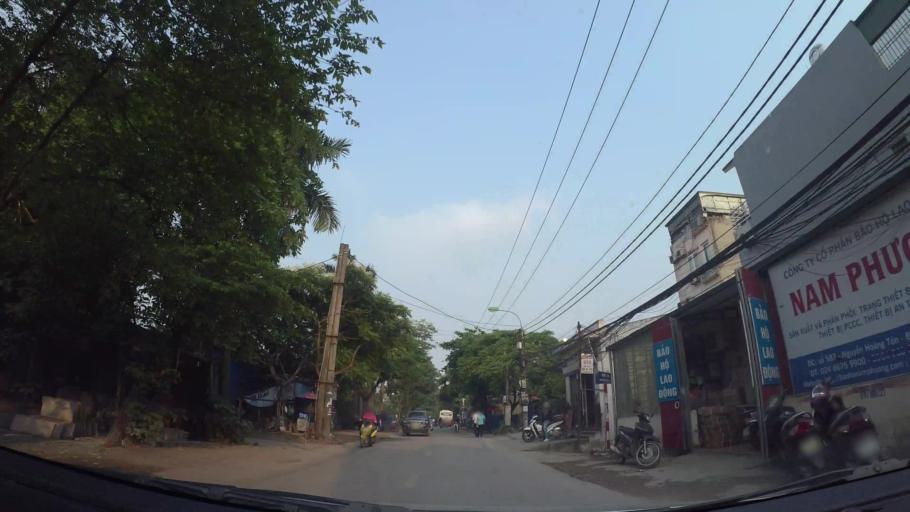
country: VN
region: Ha Noi
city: Tay Ho
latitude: 21.0762
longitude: 105.7937
